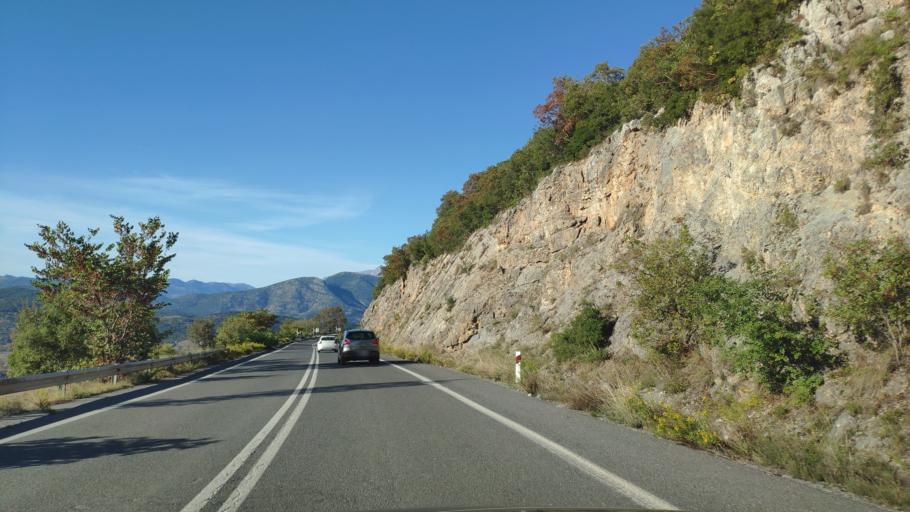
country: GR
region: Peloponnese
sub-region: Nomos Arkadias
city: Langadhia
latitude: 37.7214
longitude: 22.2025
